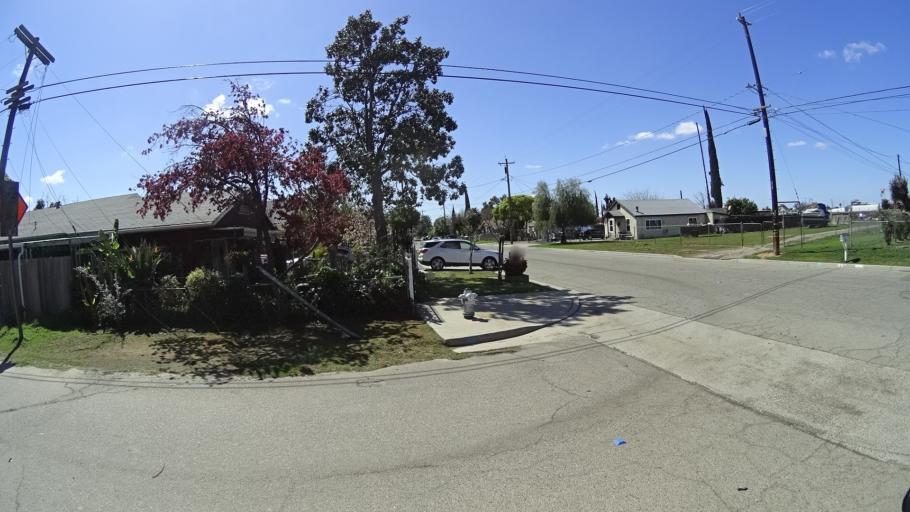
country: US
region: California
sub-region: Fresno County
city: West Park
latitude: 36.8120
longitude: -119.8872
